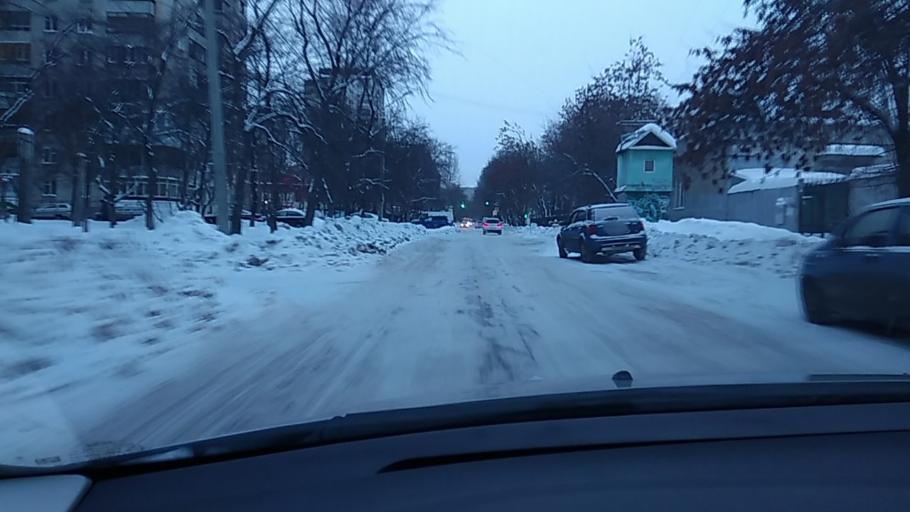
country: RU
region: Sverdlovsk
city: Yekaterinburg
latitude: 56.8968
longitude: 60.6012
